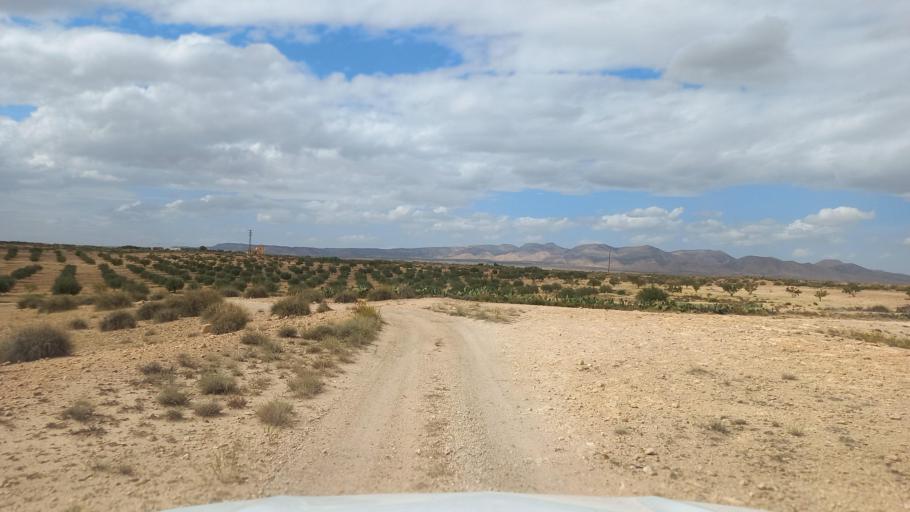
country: TN
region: Al Qasrayn
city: Sbiba
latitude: 35.3794
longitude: 9.1002
